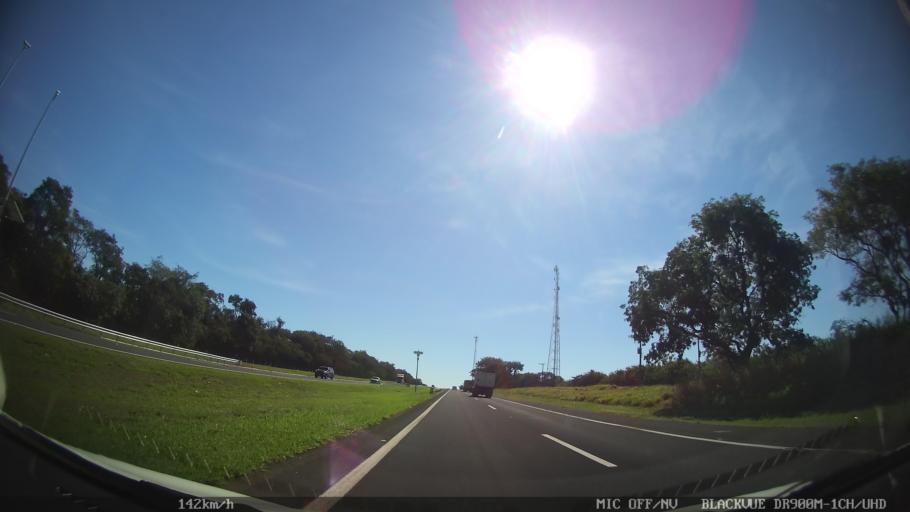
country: BR
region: Sao Paulo
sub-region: Sao Simao
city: Sao Simao
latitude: -21.6226
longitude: -47.6149
